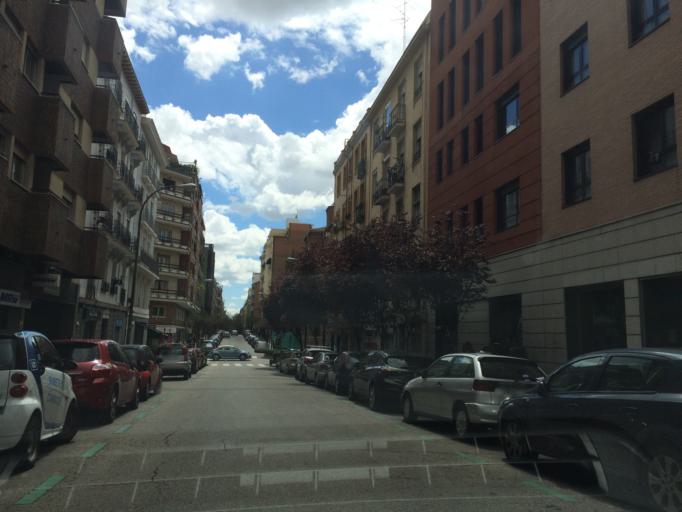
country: ES
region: Madrid
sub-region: Provincia de Madrid
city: Chamberi
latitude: 40.4447
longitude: -3.6988
